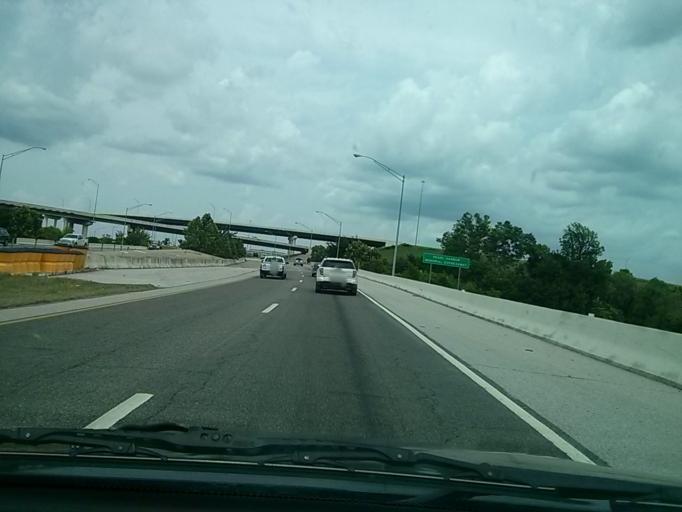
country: US
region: Oklahoma
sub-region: Tulsa County
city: Broken Arrow
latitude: 36.0269
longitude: -95.8649
